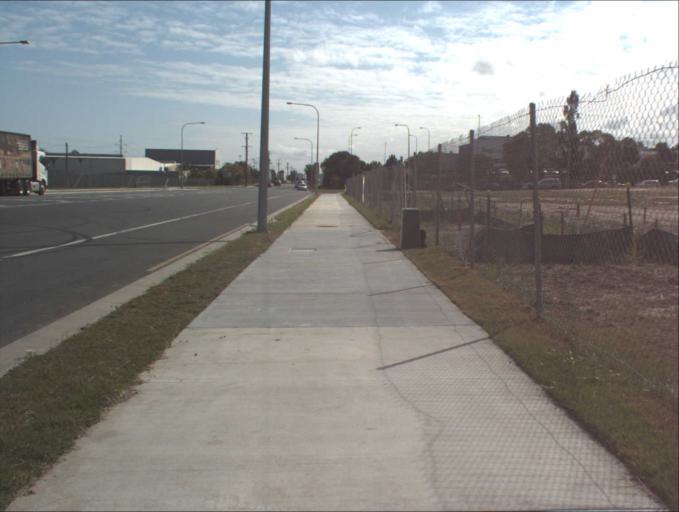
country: AU
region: Queensland
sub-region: Logan
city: Logan Reserve
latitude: -27.6882
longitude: 153.0698
